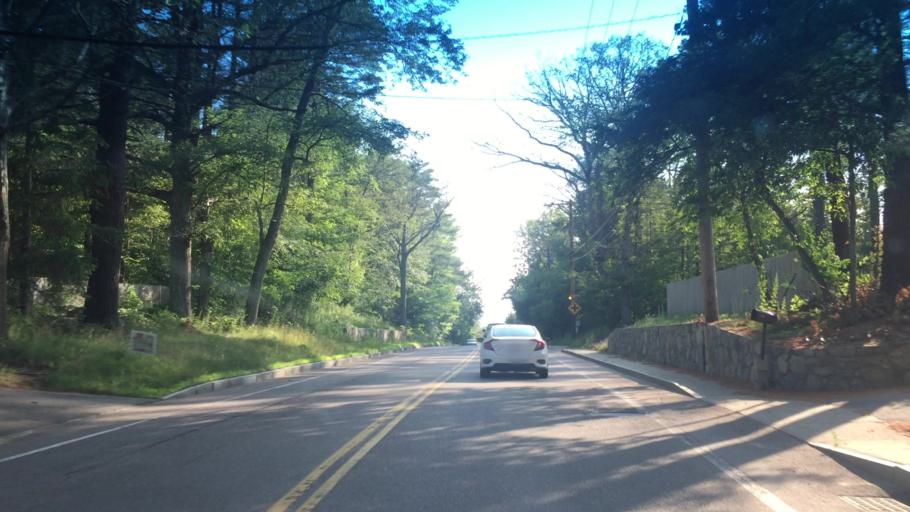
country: US
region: Massachusetts
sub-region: Norfolk County
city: Medfield
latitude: 42.1885
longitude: -71.3169
